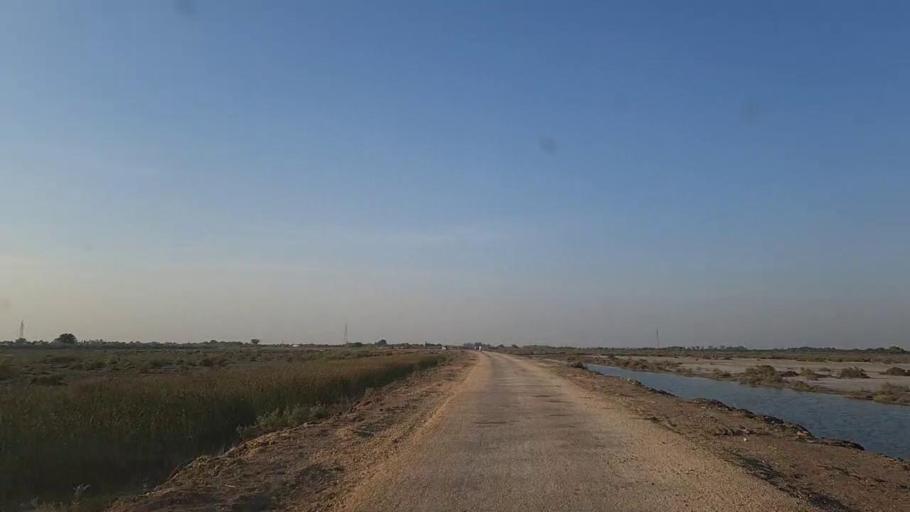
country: PK
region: Sindh
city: Mirpur Batoro
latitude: 24.6881
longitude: 68.2034
